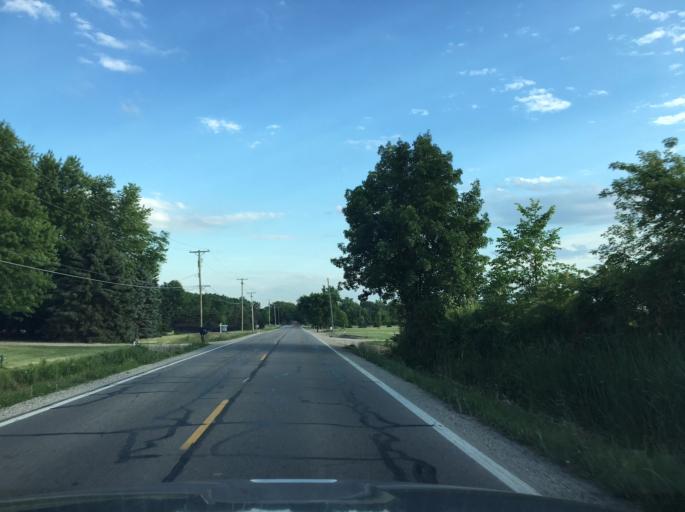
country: US
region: Michigan
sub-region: Macomb County
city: Romeo
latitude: 42.7584
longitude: -82.9610
